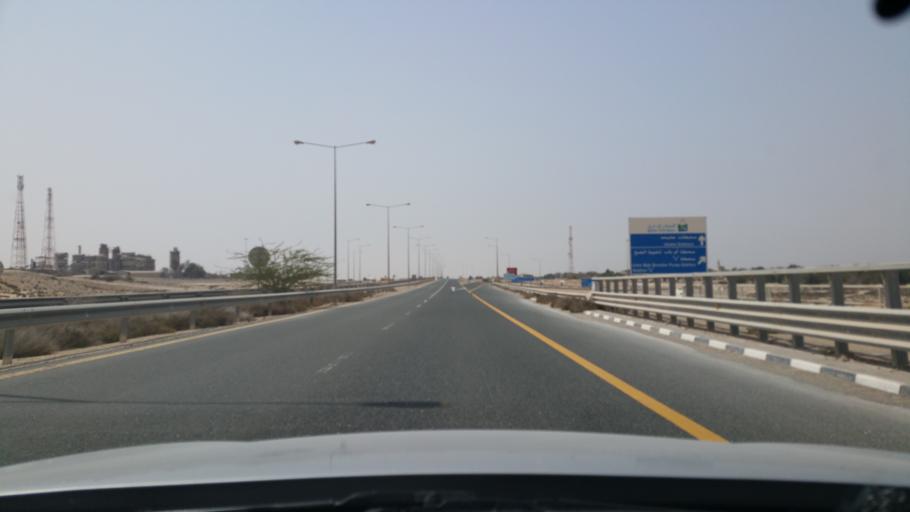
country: QA
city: Umm Bab
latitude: 25.2148
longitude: 50.8069
